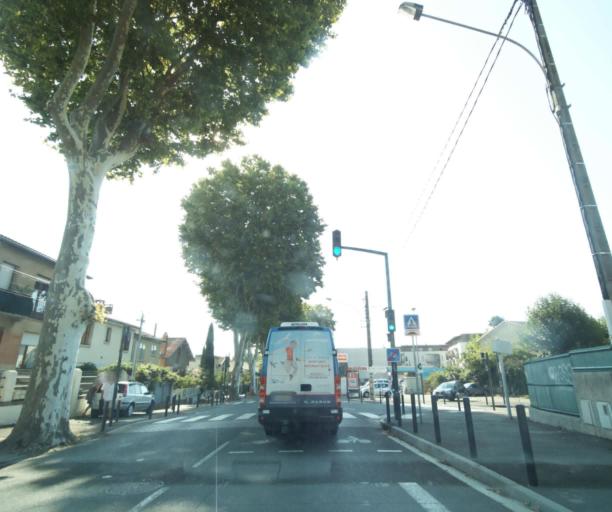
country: FR
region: Midi-Pyrenees
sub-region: Departement de la Haute-Garonne
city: Balma
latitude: 43.5950
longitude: 1.4880
